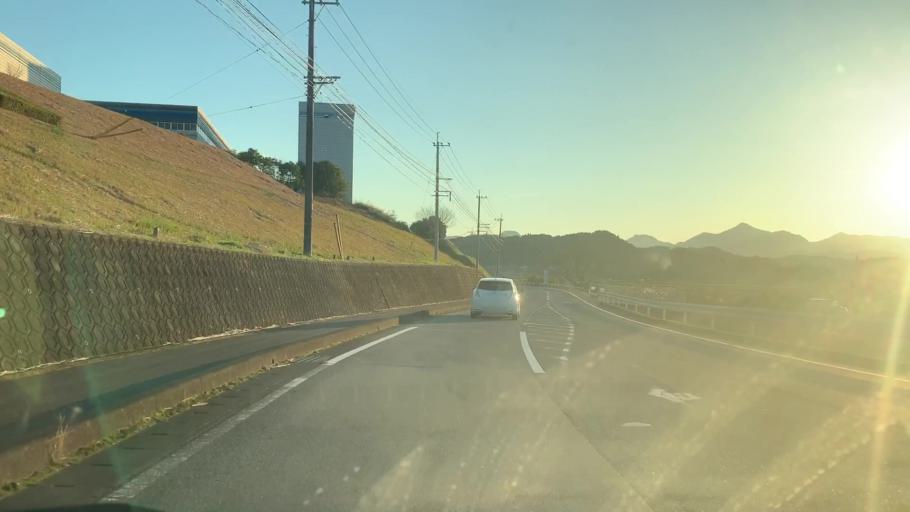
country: JP
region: Saga Prefecture
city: Imaricho-ko
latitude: 33.2795
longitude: 129.9664
